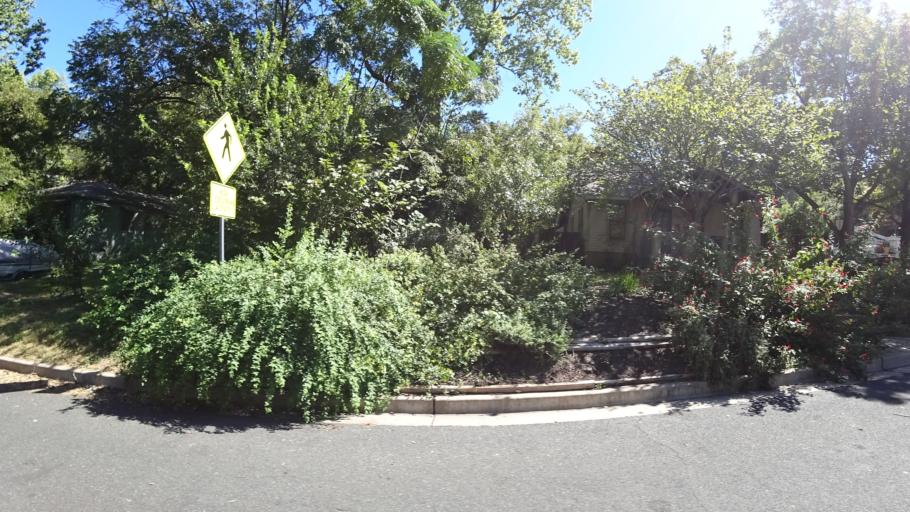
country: US
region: Texas
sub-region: Travis County
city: Austin
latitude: 30.2457
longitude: -97.7435
